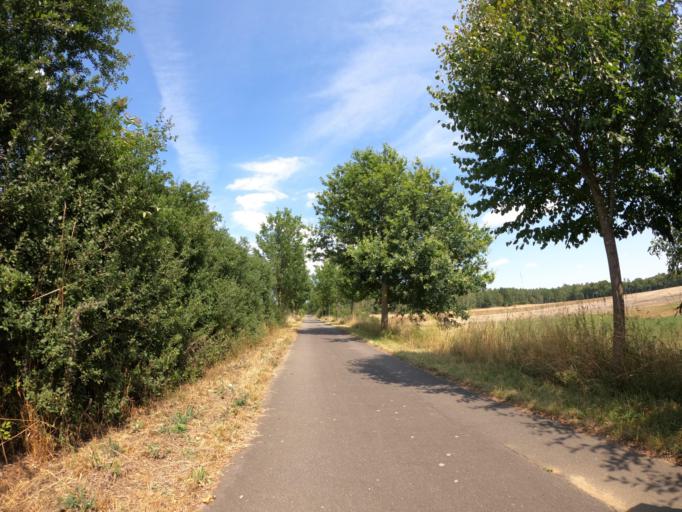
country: DE
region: Mecklenburg-Vorpommern
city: Woldegk
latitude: 53.3085
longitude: 13.5737
